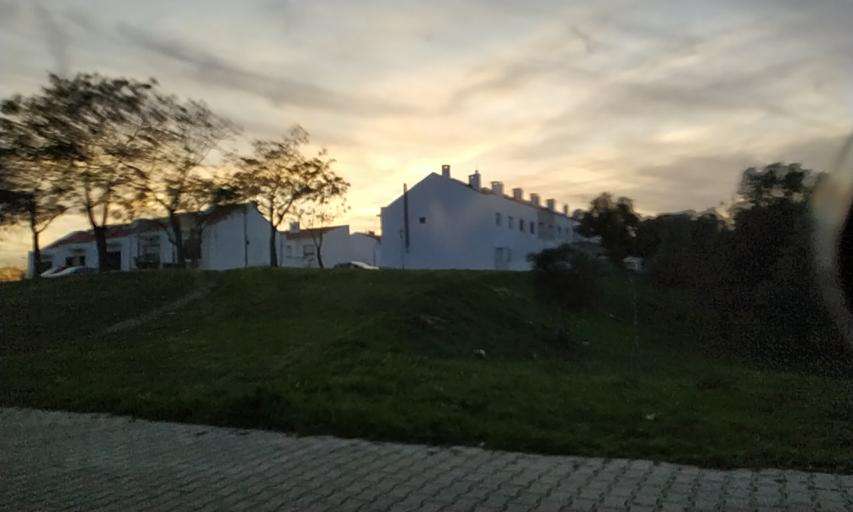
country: PT
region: Setubal
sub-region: Setubal
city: Setubal
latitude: 38.5221
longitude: -8.8469
